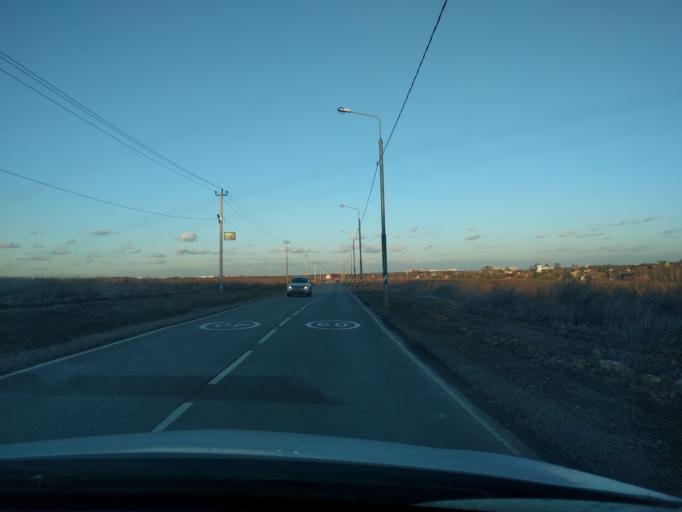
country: RU
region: Moskovskaya
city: Dubrovitsy
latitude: 55.4915
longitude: 37.4178
